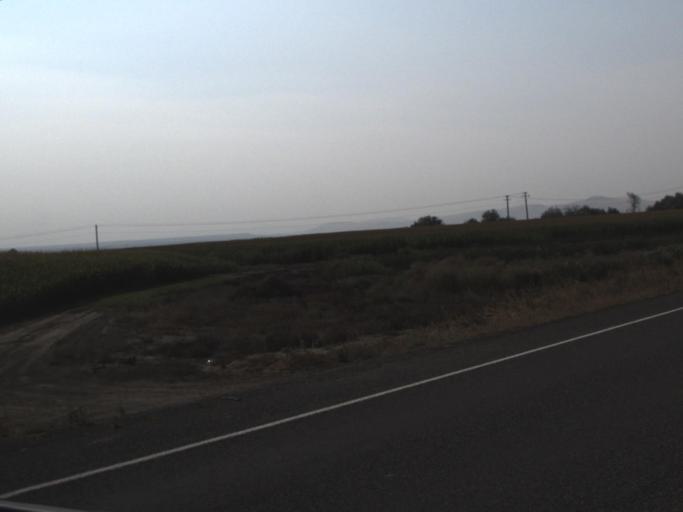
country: US
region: Washington
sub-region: Yakima County
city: Granger
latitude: 46.2517
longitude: -120.1221
